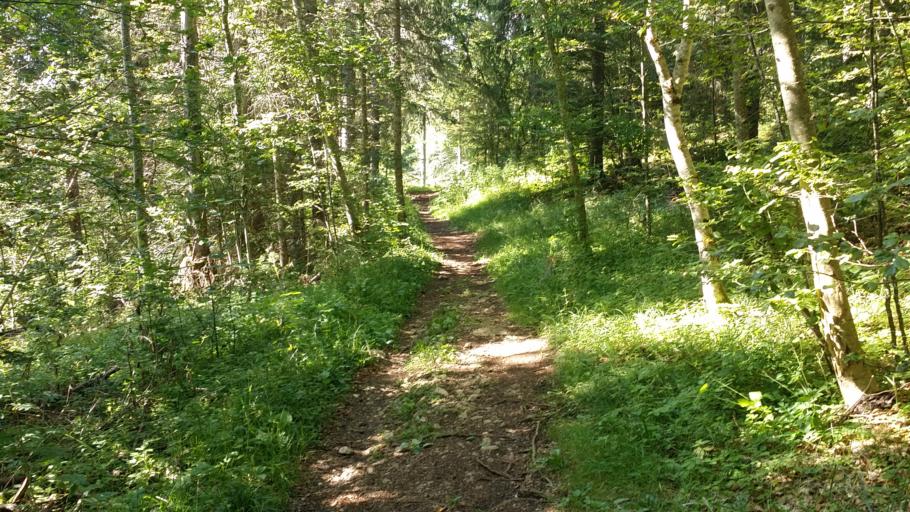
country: FR
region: Franche-Comte
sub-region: Departement du Jura
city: Les Rousses
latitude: 46.4736
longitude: 6.0532
